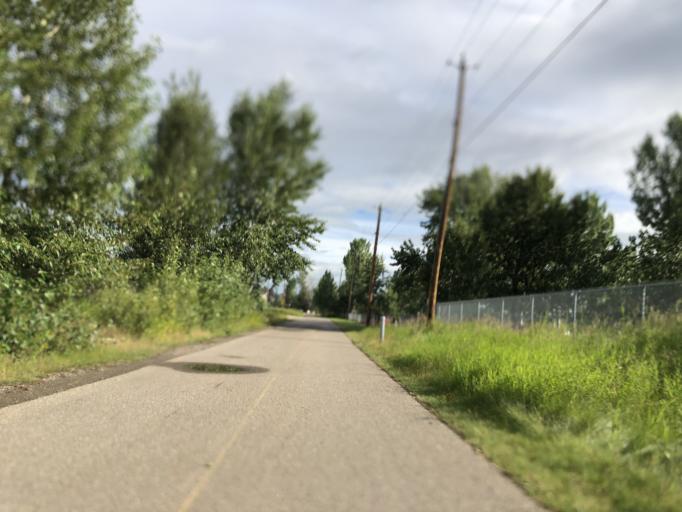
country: CA
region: Alberta
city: Calgary
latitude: 51.0294
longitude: -114.0113
